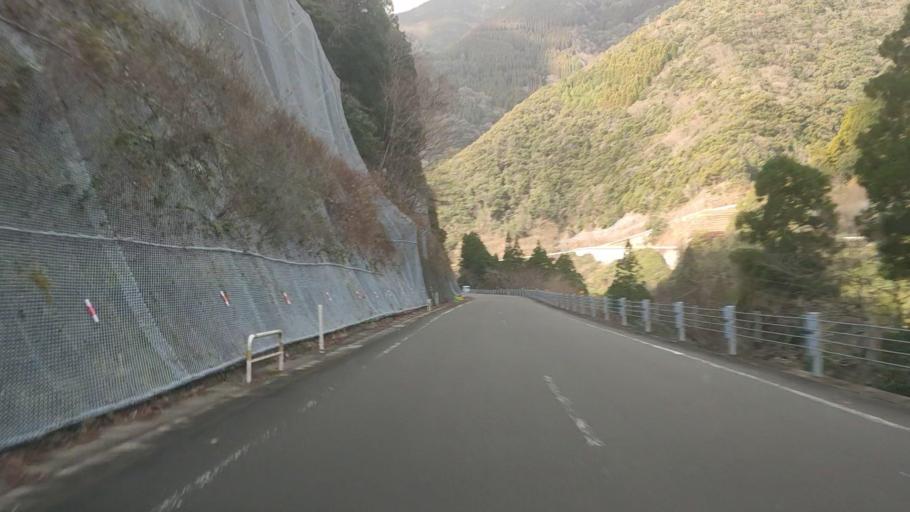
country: JP
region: Kumamoto
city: Hitoyoshi
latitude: 32.4105
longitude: 130.8360
